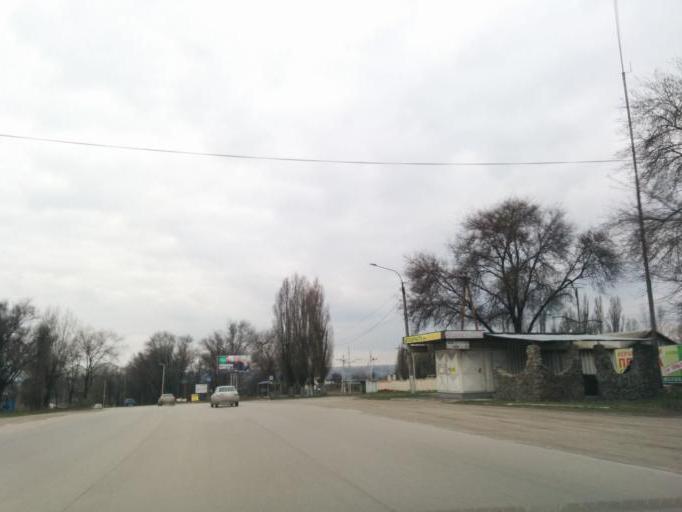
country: RU
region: Rostov
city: Novocherkassk
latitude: 47.4650
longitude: 40.0996
